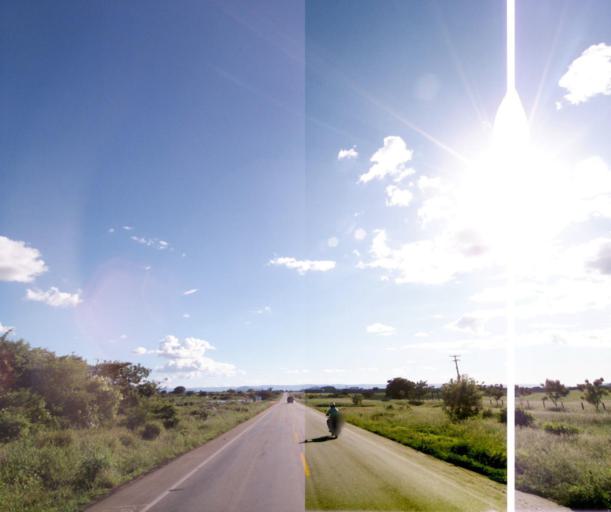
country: BR
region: Bahia
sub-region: Guanambi
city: Guanambi
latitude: -14.1723
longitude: -42.7268
